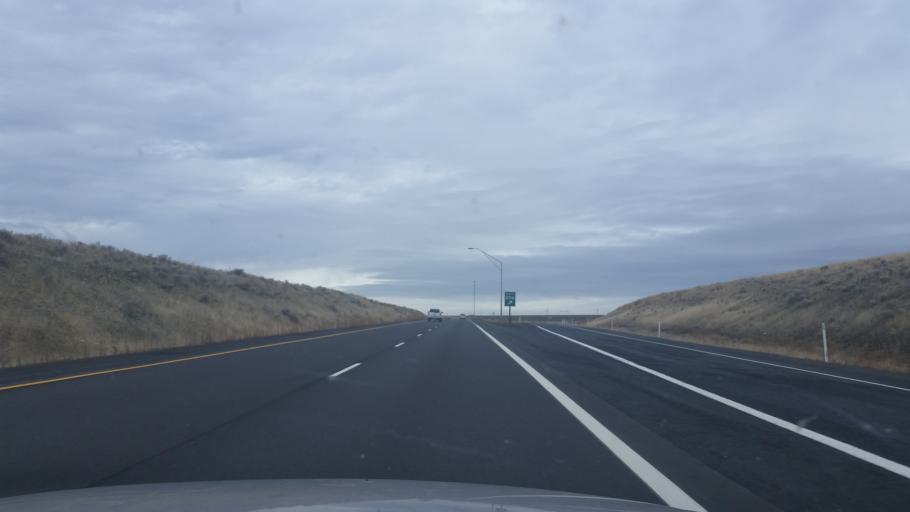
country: US
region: Washington
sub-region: Adams County
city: Ritzville
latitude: 47.0972
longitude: -118.6617
